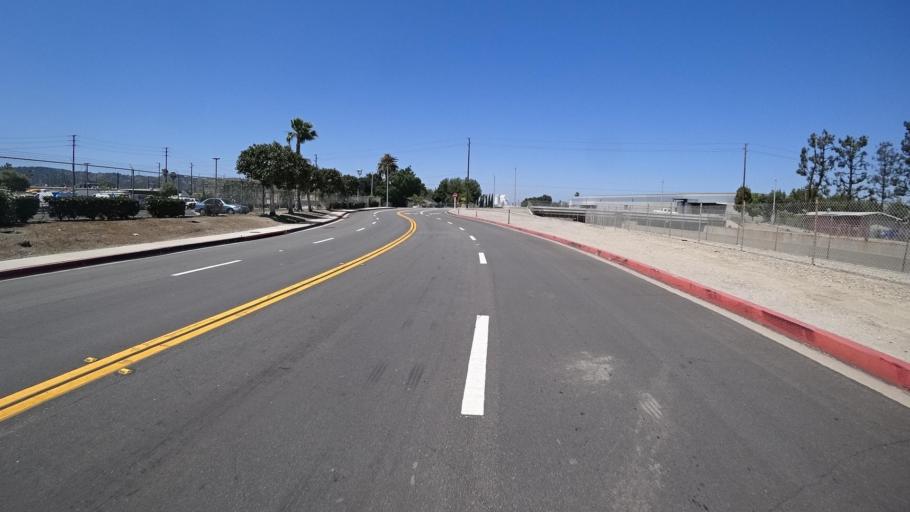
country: US
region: California
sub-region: Los Angeles County
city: La Puente
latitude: 34.0201
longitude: -117.9706
